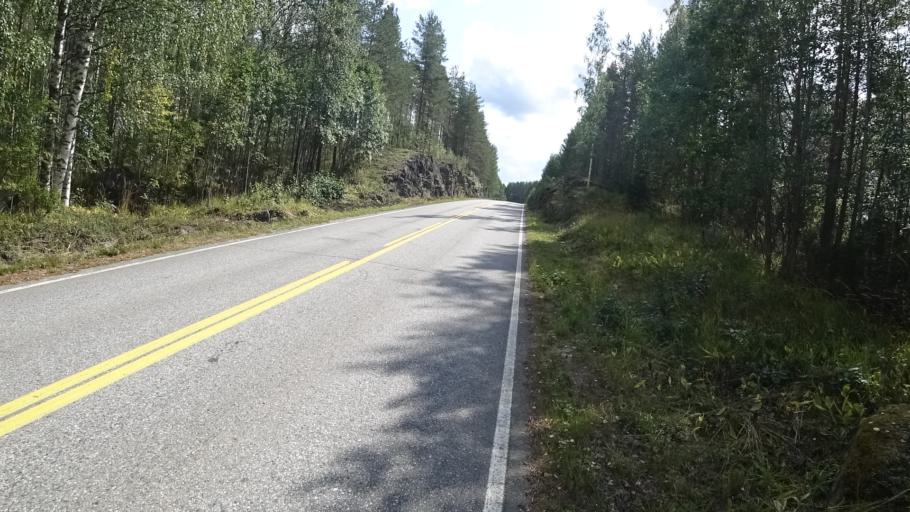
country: FI
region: North Karelia
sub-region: Joensuu
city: Ilomantsi
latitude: 62.6206
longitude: 31.1998
